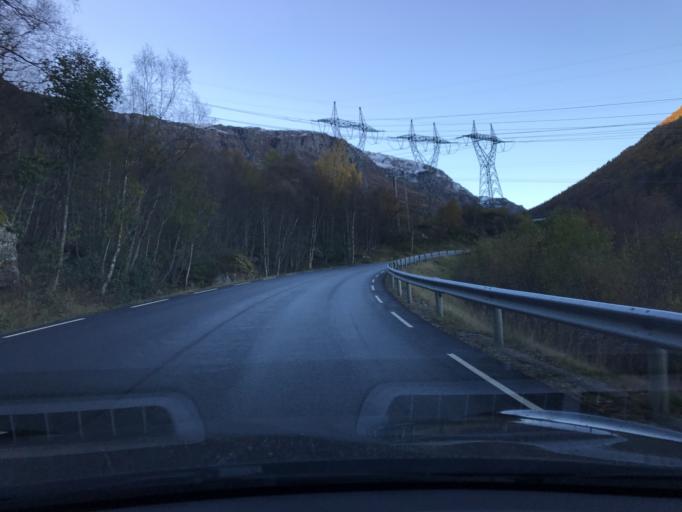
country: NO
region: Sogn og Fjordane
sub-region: Aurland
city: Aurlandsvangen
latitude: 60.8524
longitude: 7.3152
